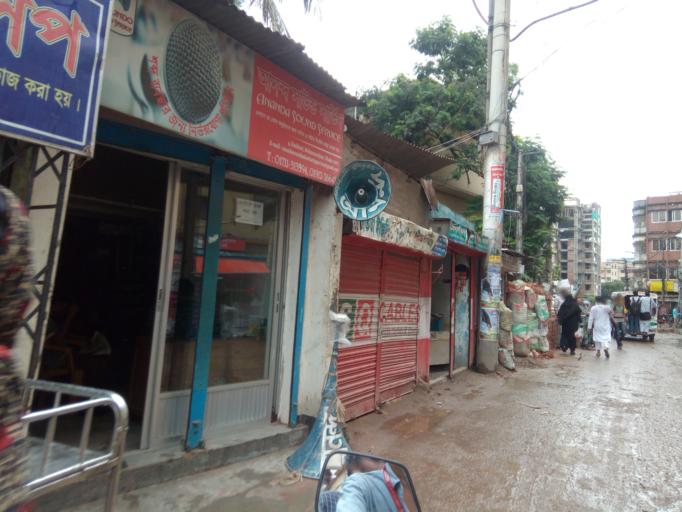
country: BD
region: Dhaka
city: Azimpur
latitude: 23.7573
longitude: 90.3607
